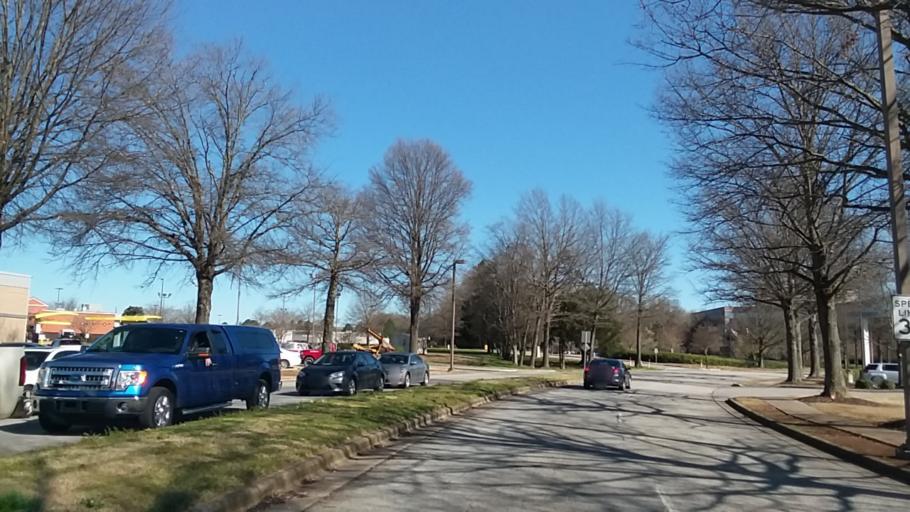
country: US
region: Alabama
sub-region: Madison County
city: Redstone Arsenal
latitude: 34.7437
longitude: -86.6744
